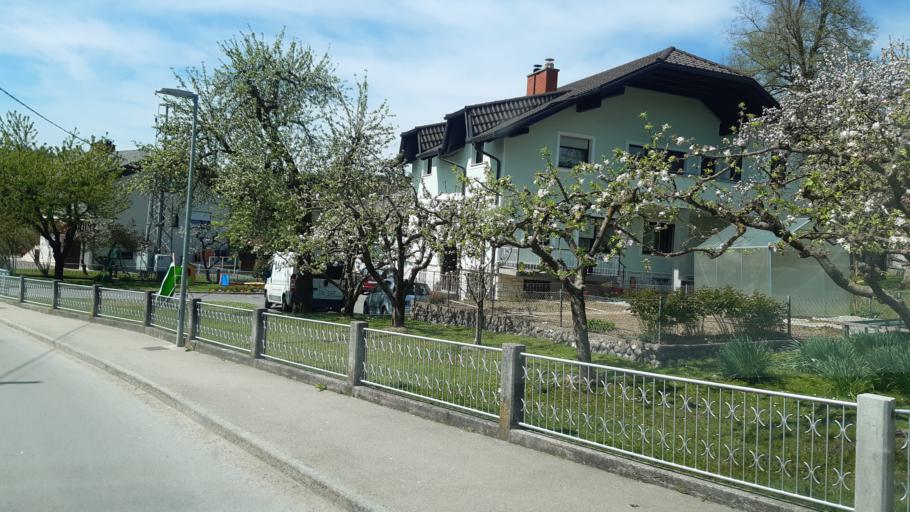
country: SI
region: Domzale
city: Radomlje
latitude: 46.1808
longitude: 14.6314
